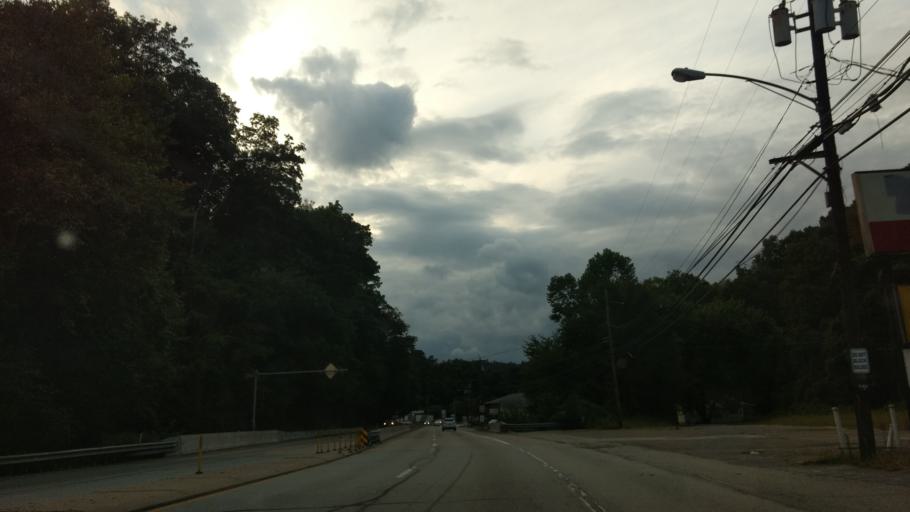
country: US
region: Pennsylvania
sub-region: Allegheny County
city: Elizabeth
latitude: 40.2660
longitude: -79.8799
